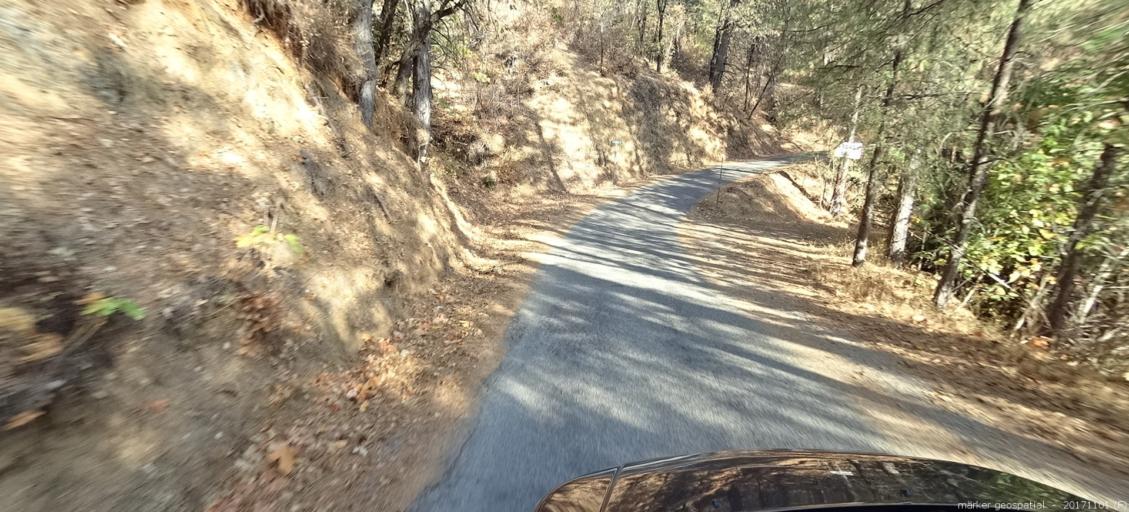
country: US
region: California
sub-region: Shasta County
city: Shasta Lake
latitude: 40.8123
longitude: -122.3108
